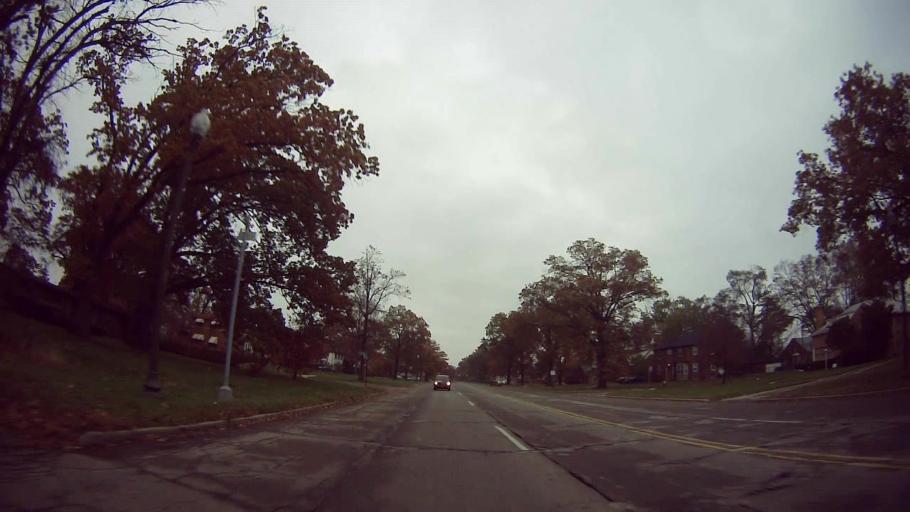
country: US
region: Michigan
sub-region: Oakland County
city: Oak Park
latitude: 42.4350
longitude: -83.1651
